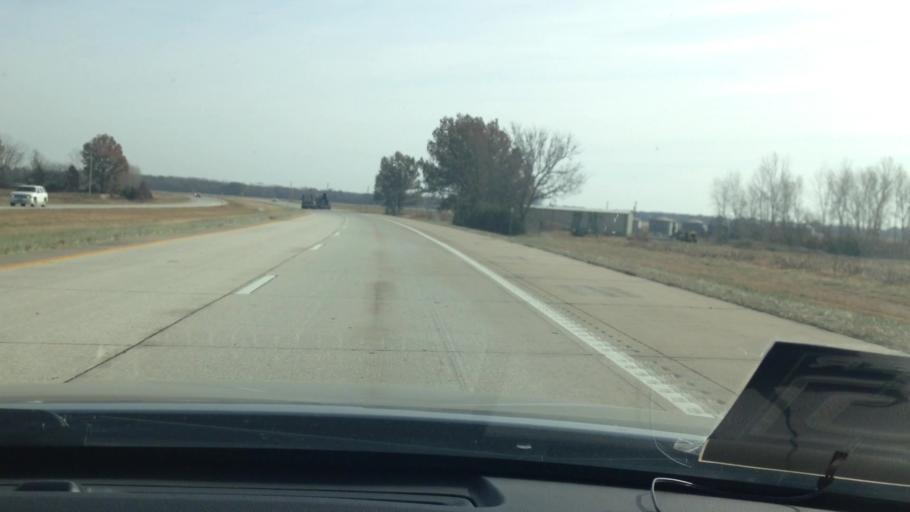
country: US
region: Missouri
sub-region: Henry County
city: Clinton
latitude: 38.4300
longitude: -93.9240
